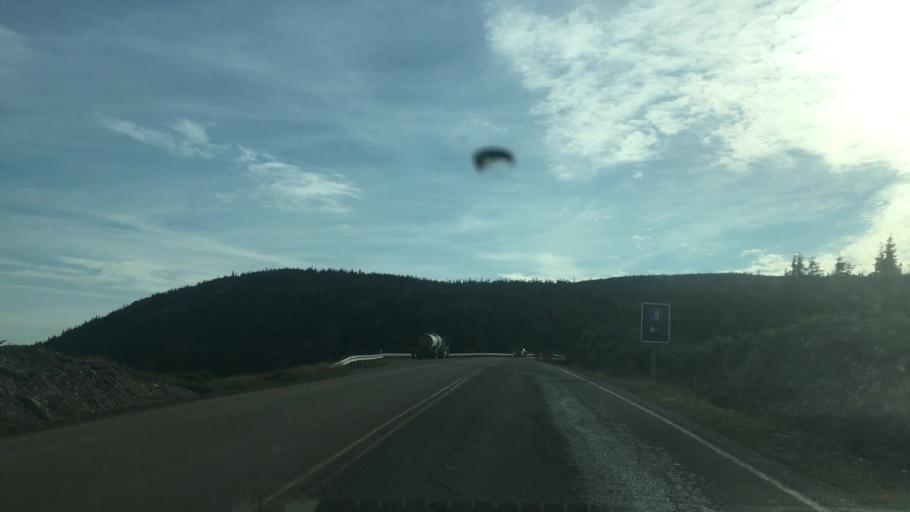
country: CA
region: Nova Scotia
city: Sydney Mines
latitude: 46.8184
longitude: -60.8332
